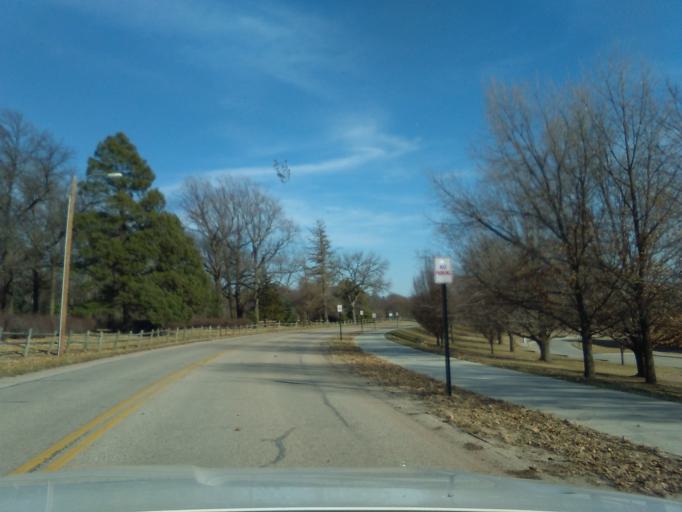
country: US
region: Nebraska
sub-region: Otoe County
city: Nebraska City
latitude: 40.6796
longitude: -95.8801
